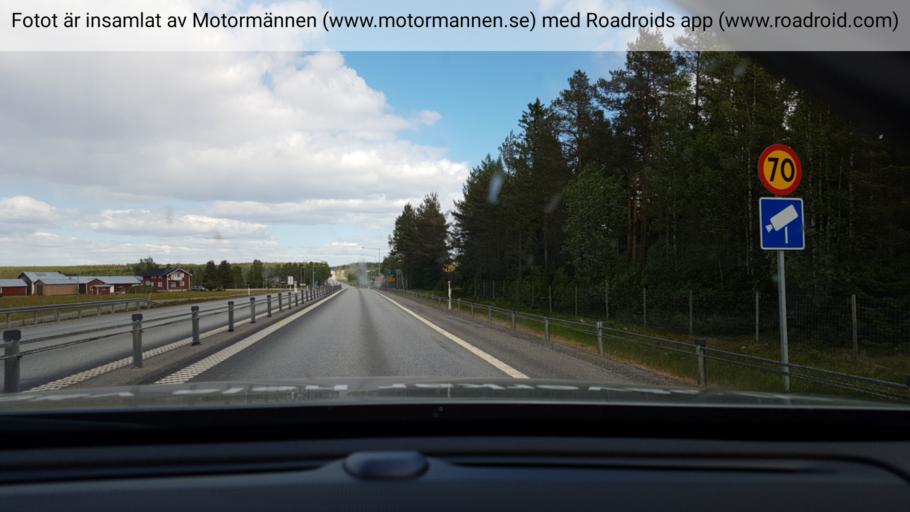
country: SE
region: Vaesterbotten
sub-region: Umea Kommun
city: Hoernefors
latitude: 63.6776
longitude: 19.9926
